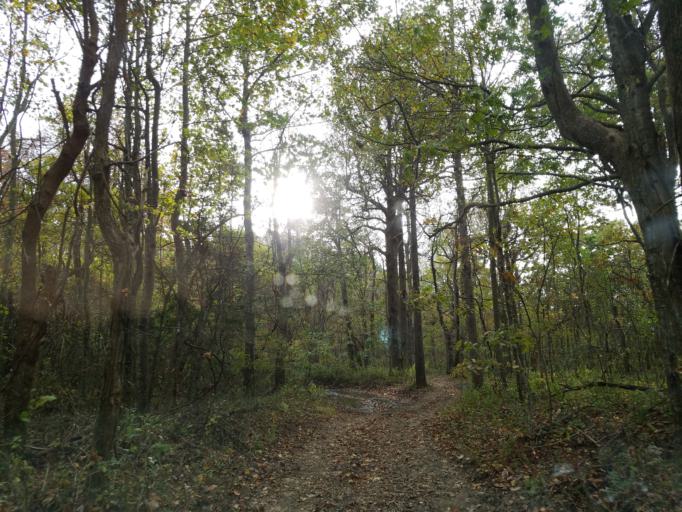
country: US
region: Georgia
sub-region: Dawson County
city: Dawsonville
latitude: 34.6004
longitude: -84.2229
